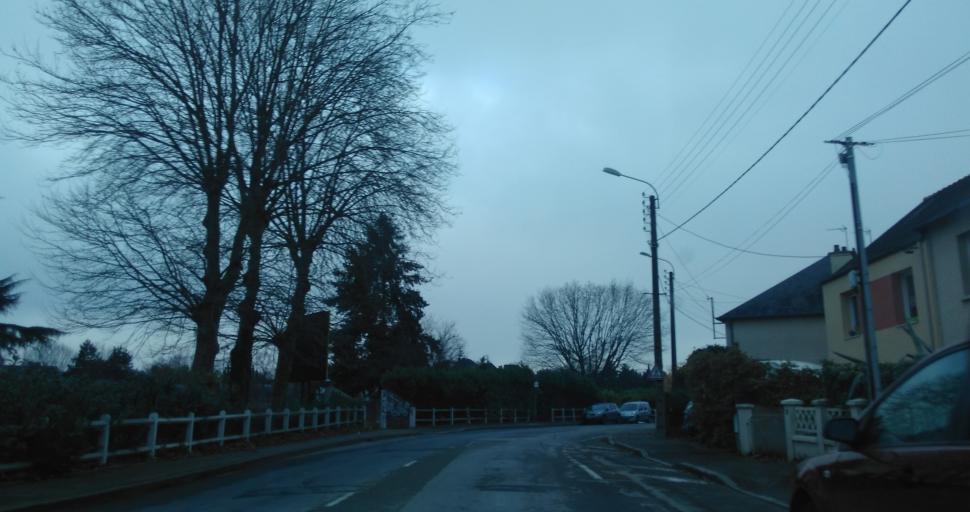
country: FR
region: Brittany
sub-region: Departement d'Ille-et-Vilaine
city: Rennes
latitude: 48.1301
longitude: -1.6739
